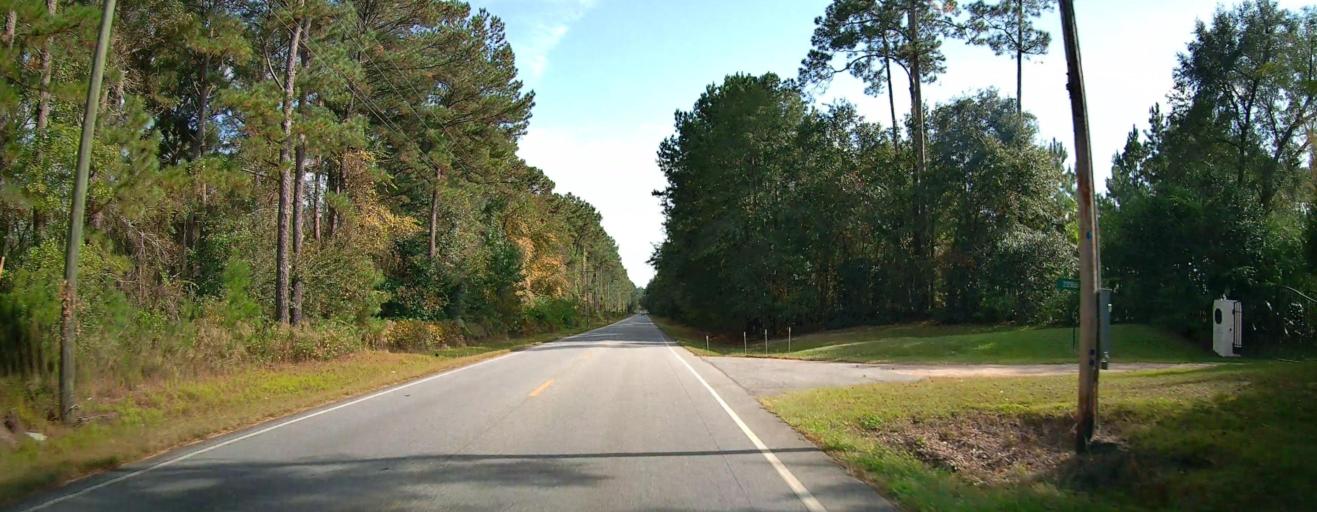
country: US
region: Georgia
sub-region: Thomas County
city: Thomasville
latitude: 30.9290
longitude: -84.0206
